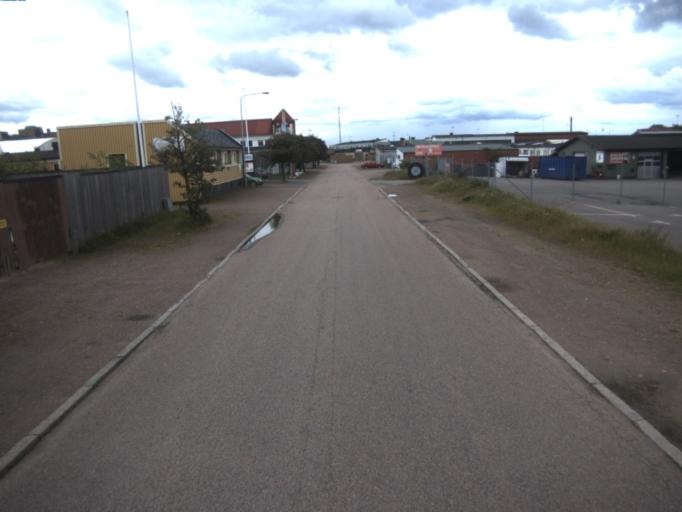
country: SE
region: Skane
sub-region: Helsingborg
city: Helsingborg
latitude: 56.0330
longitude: 12.7141
